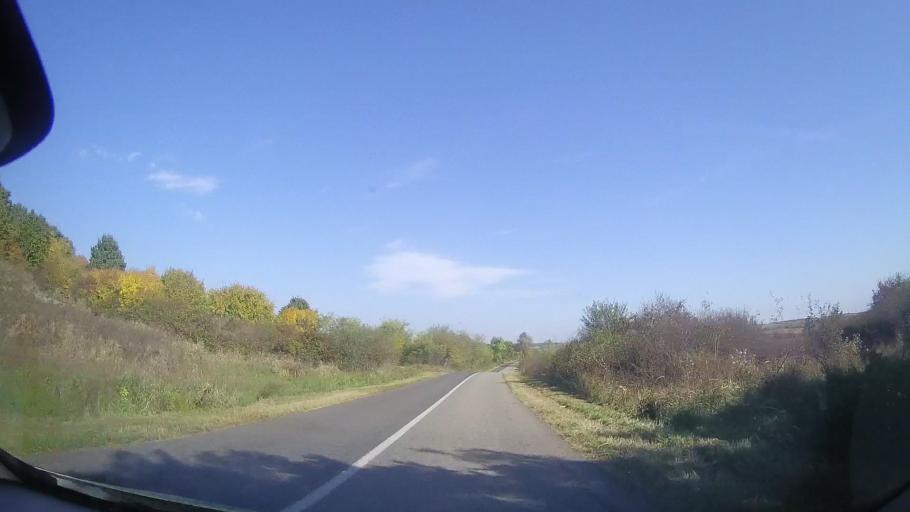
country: RO
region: Timis
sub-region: Comuna Ghizela
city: Ghizela
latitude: 45.8173
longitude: 21.7252
